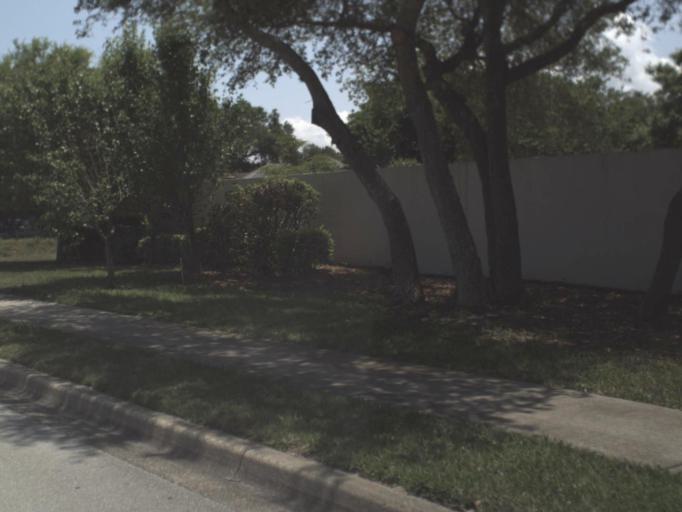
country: US
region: Florida
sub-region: Saint Johns County
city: Saint Augustine Beach
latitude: 29.8524
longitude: -81.2789
